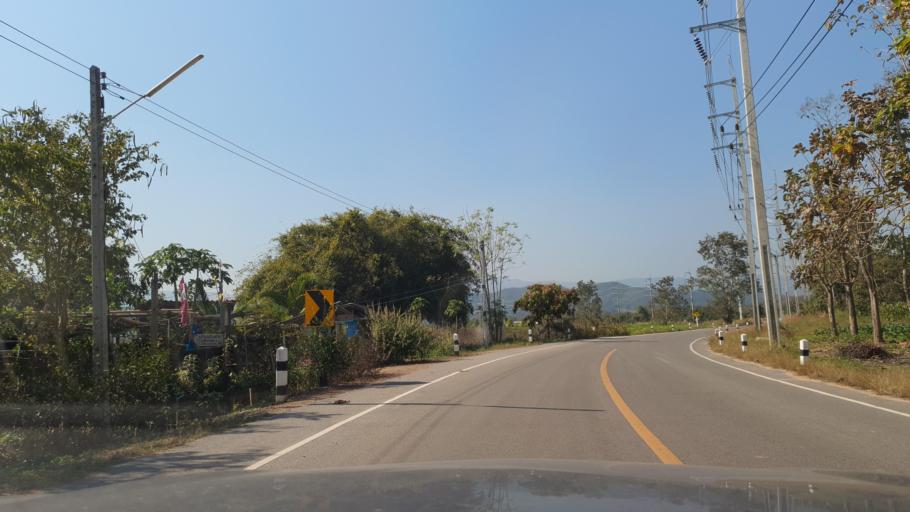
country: TH
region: Chiang Rai
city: Mae Lao
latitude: 19.8002
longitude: 99.6966
